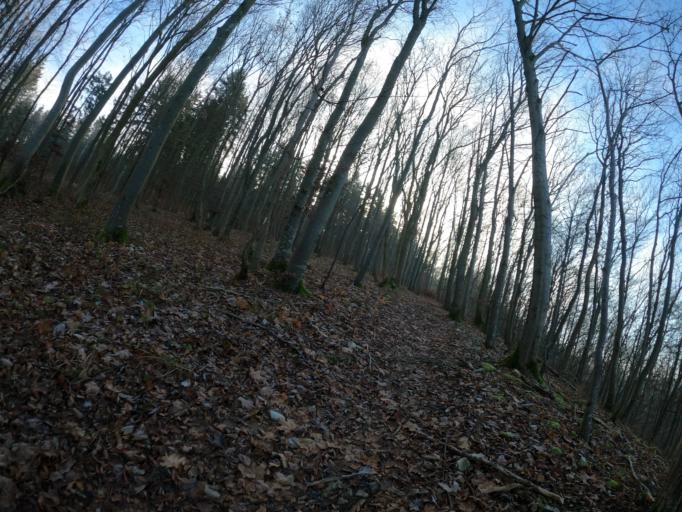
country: DE
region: Baden-Wuerttemberg
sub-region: Regierungsbezirk Stuttgart
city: Deggingen
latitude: 48.5918
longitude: 9.7404
